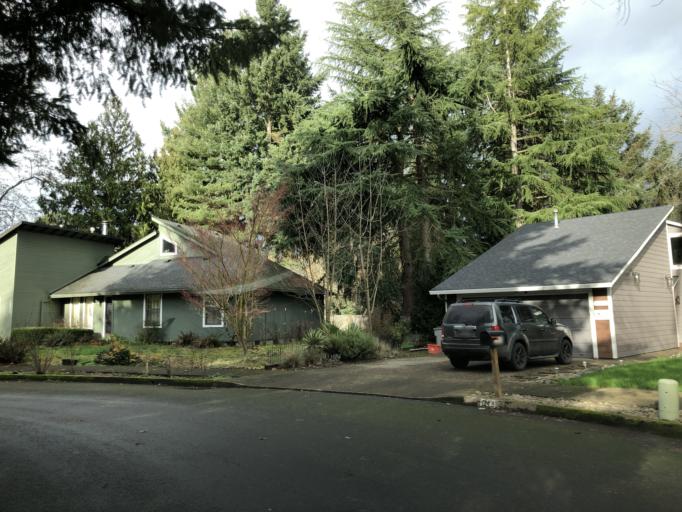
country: US
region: Oregon
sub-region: Washington County
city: Tigard
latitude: 45.4259
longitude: -122.7843
